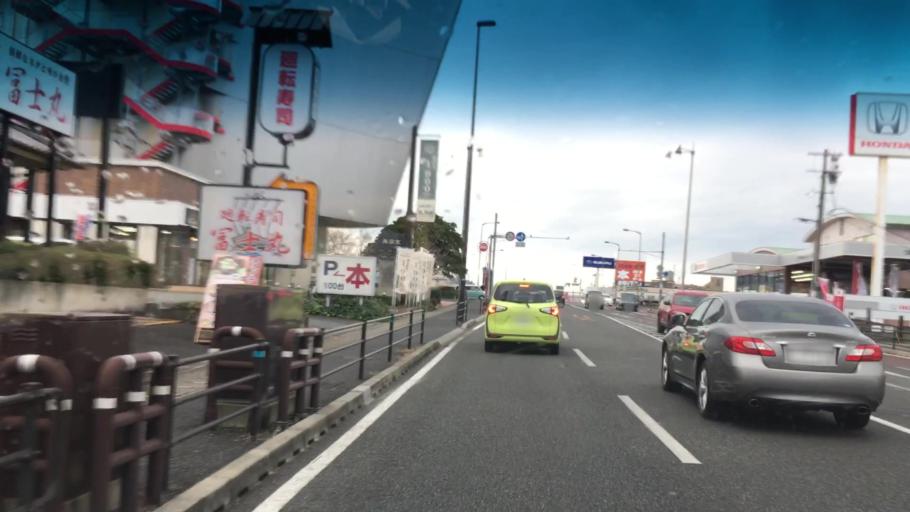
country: JP
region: Fukuoka
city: Fukuoka-shi
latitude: 33.5682
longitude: 130.3283
